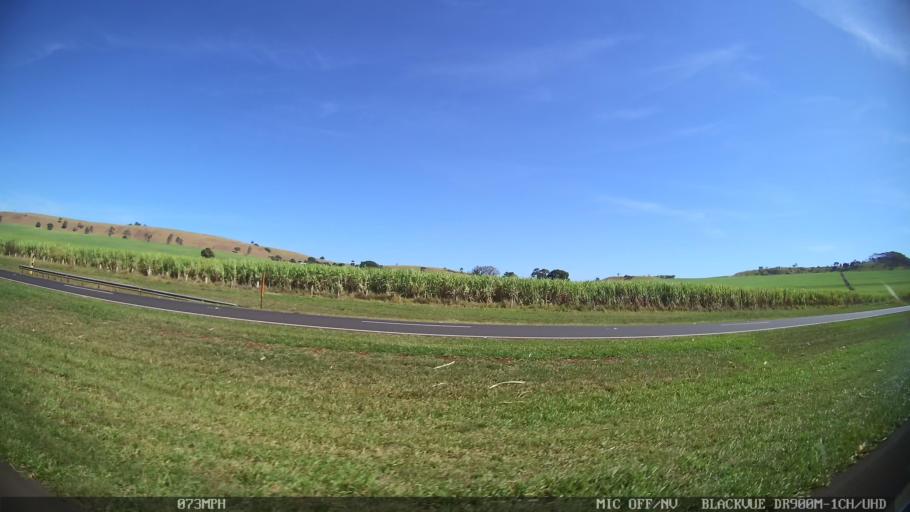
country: BR
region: Sao Paulo
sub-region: Sao Simao
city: Sao Simao
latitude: -21.4375
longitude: -47.6510
